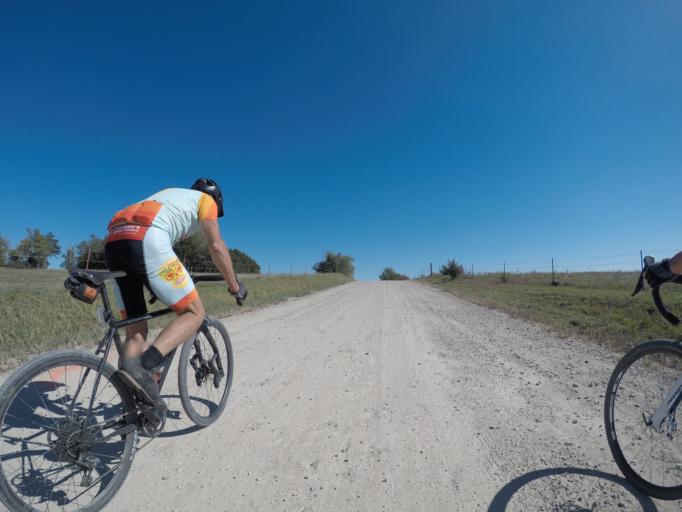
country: US
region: Kansas
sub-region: Wabaunsee County
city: Alma
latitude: 39.0685
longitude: -96.3537
